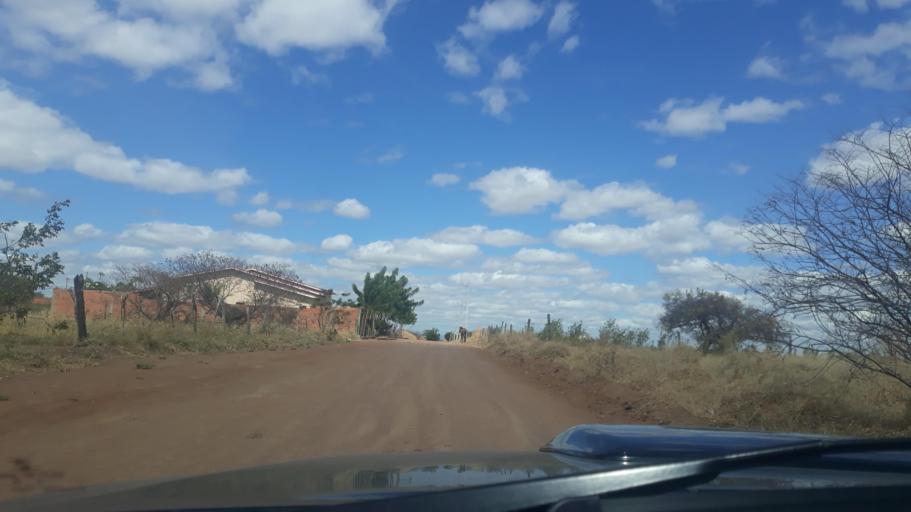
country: BR
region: Bahia
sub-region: Riacho De Santana
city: Riacho de Santana
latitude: -13.8986
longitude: -42.8515
